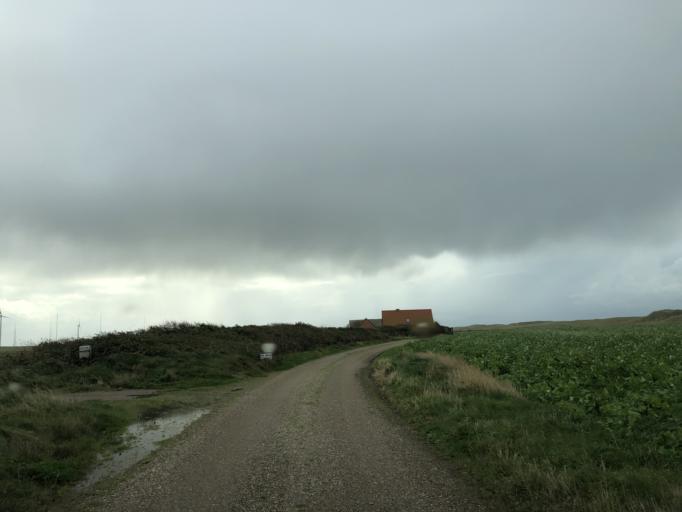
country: DK
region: Central Jutland
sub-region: Lemvig Kommune
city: Harboore
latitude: 56.4680
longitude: 8.1297
